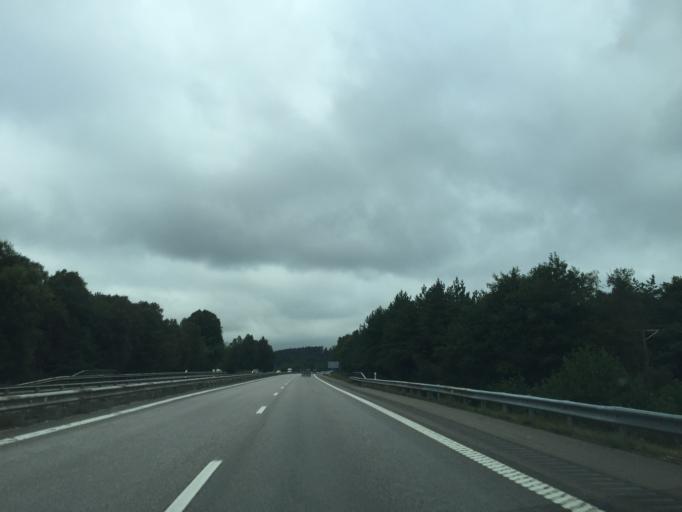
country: SE
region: Halland
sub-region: Kungsbacka Kommun
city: Frillesas
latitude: 57.3790
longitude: 12.1963
